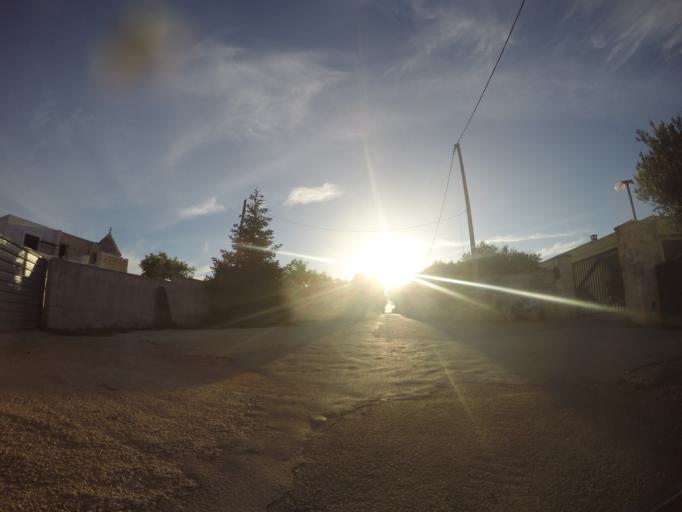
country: IT
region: Apulia
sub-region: Provincia di Taranto
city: Martina Franca
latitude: 40.6508
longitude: 17.3632
